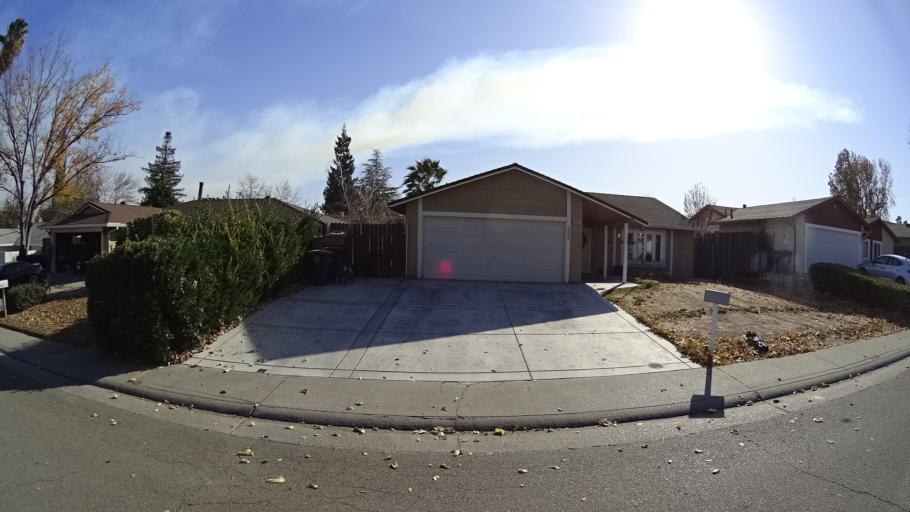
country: US
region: California
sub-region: Sacramento County
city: Antelope
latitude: 38.7018
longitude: -121.3223
